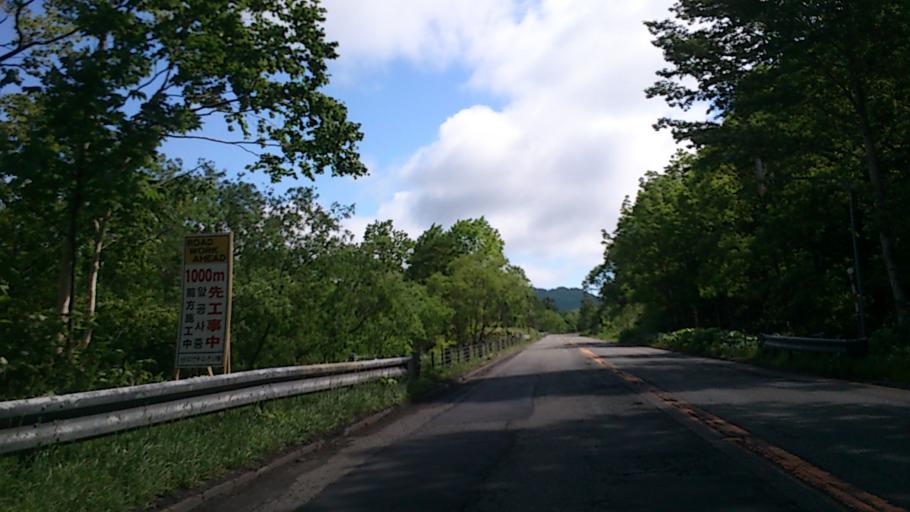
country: JP
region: Hokkaido
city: Shiraoi
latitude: 42.7152
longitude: 141.2010
